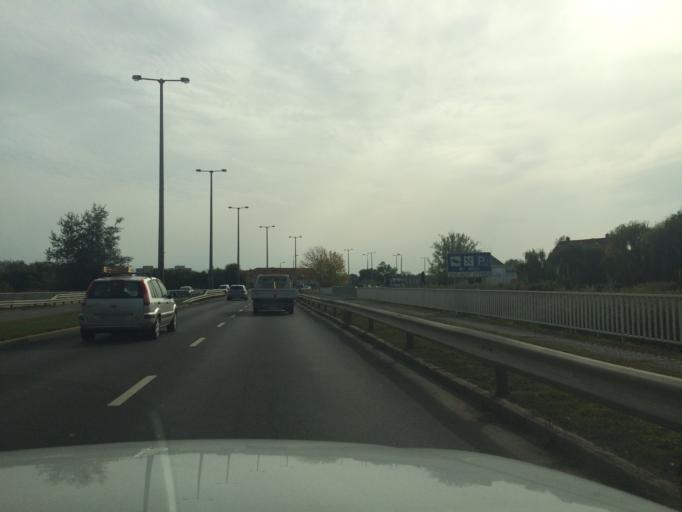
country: HU
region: Szabolcs-Szatmar-Bereg
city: Nyiregyhaza
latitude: 47.9613
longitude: 21.7269
